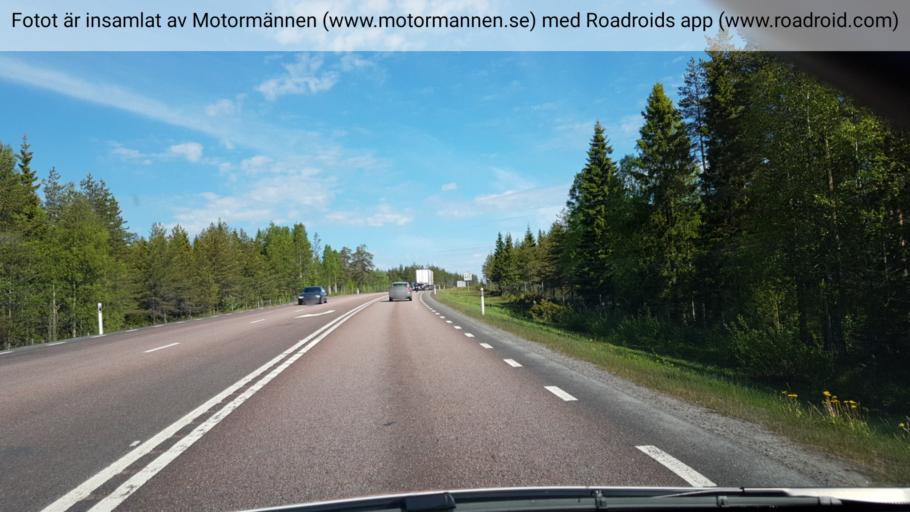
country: SE
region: Vaesterbotten
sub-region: Skelleftea Kommun
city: Burea
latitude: 64.4329
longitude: 21.2805
